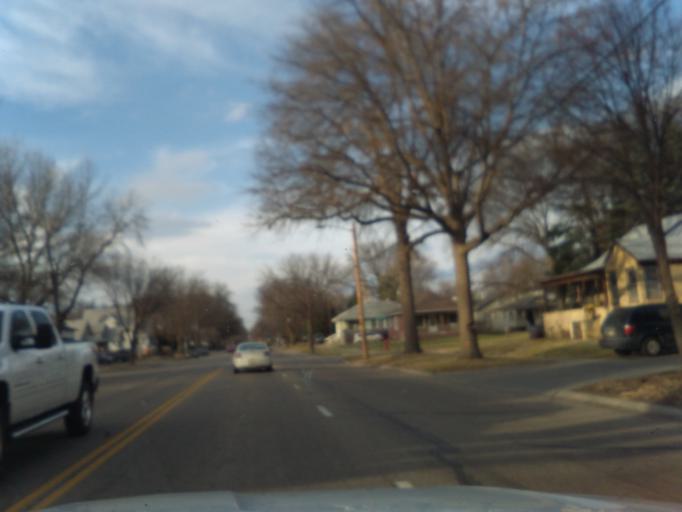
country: US
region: Nebraska
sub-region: Lancaster County
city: Lincoln
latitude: 40.7954
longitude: -96.7027
